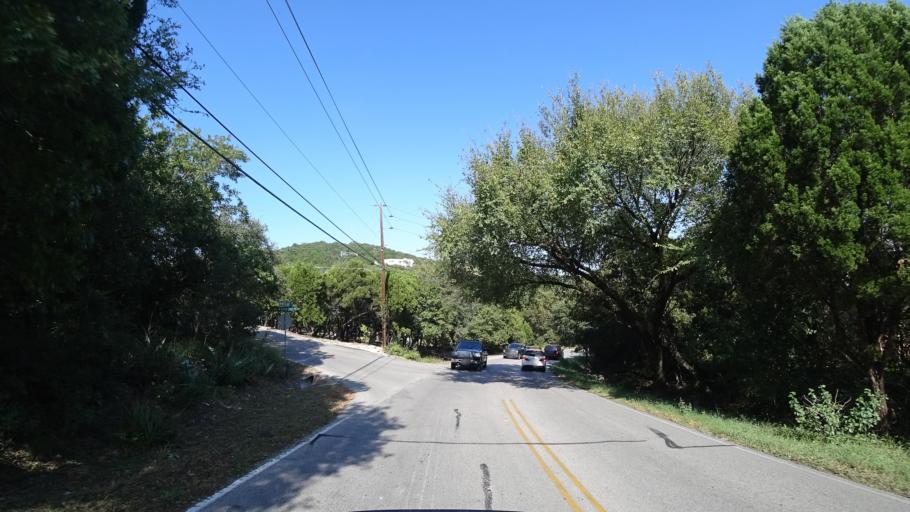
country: US
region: Texas
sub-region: Travis County
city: West Lake Hills
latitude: 30.2910
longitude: -97.8016
